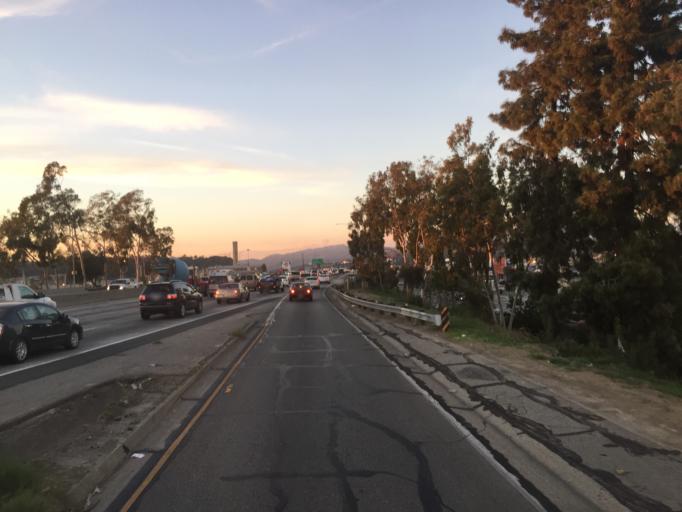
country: US
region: California
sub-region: Los Angeles County
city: Boyle Heights
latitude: 34.0596
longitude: -118.2144
